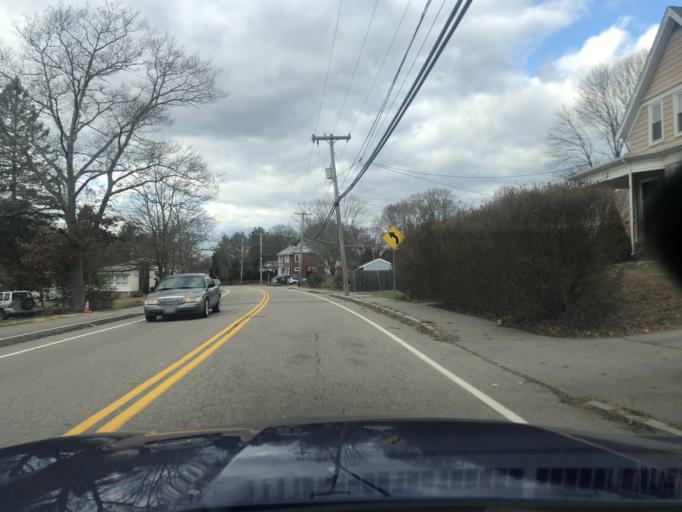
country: US
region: Massachusetts
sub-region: Plymouth County
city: Brockton
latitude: 42.1074
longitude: -71.0059
